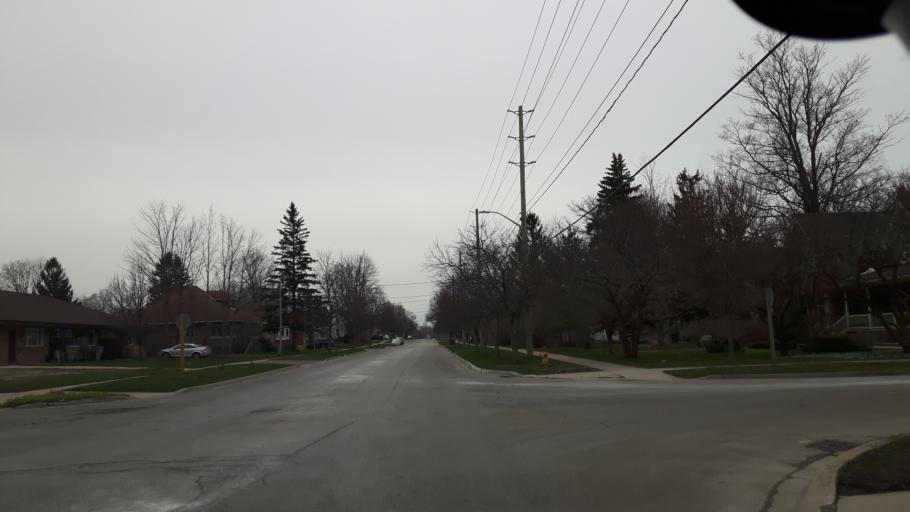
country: CA
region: Ontario
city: Goderich
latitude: 43.7458
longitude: -81.7047
